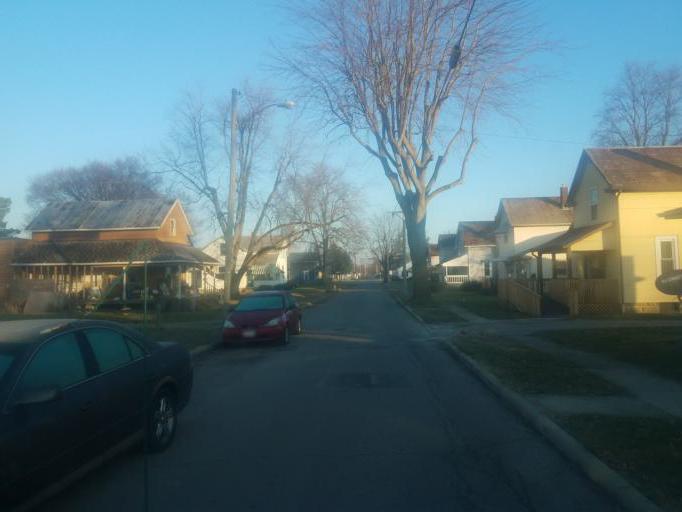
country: US
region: Ohio
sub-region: Crawford County
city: Bucyrus
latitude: 40.8185
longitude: -82.9712
